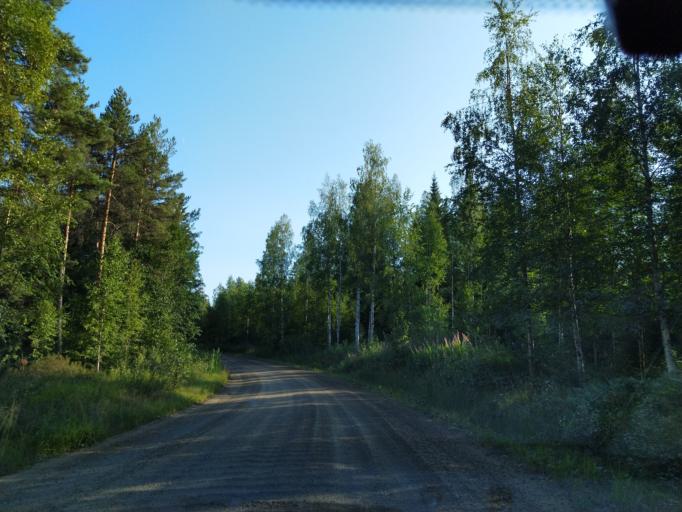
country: FI
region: Central Finland
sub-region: Jaemsae
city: Kuhmoinen
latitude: 61.6288
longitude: 25.0930
